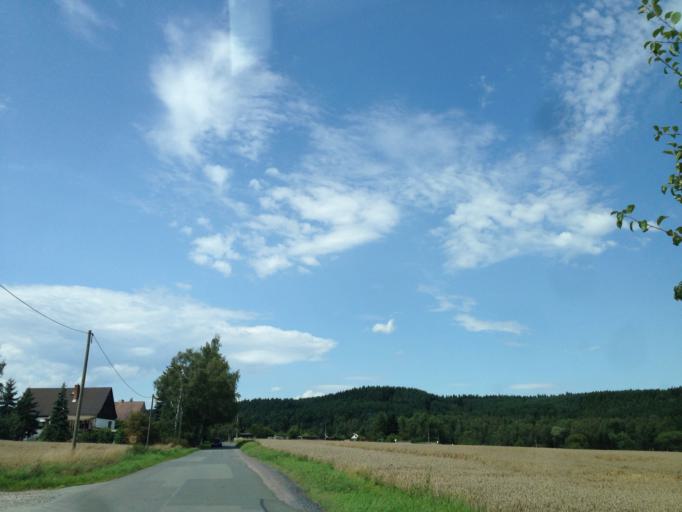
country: DE
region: Thuringia
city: Possneck
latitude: 50.7057
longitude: 11.5756
